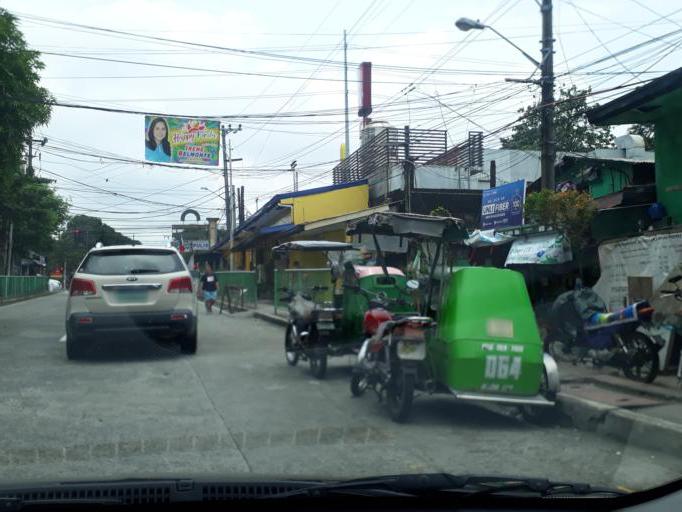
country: PH
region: Calabarzon
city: Del Monte
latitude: 14.6231
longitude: 121.0260
